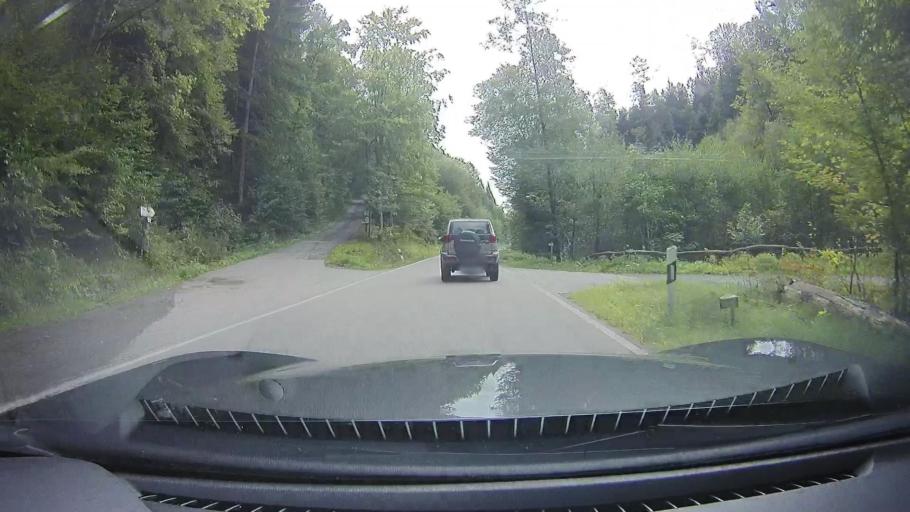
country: DE
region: Baden-Wuerttemberg
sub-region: Regierungsbezirk Stuttgart
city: Spiegelberg
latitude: 49.0461
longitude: 9.4242
